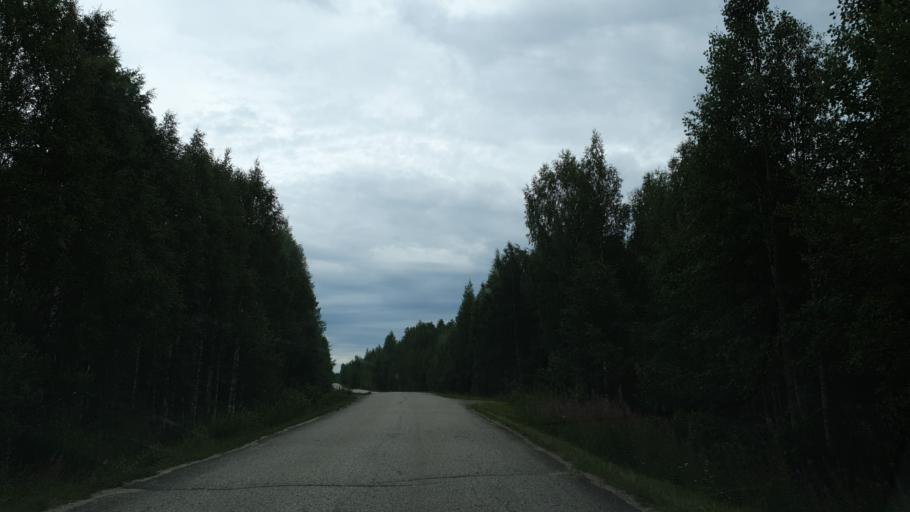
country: FI
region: Kainuu
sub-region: Kehys-Kainuu
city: Kuhmo
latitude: 64.3521
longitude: 29.0892
